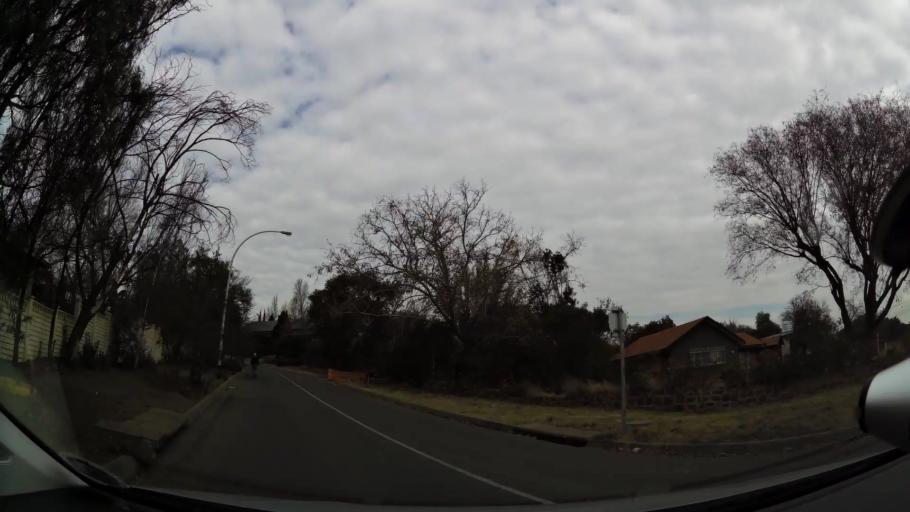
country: ZA
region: Orange Free State
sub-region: Mangaung Metropolitan Municipality
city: Bloemfontein
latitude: -29.0905
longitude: 26.2090
